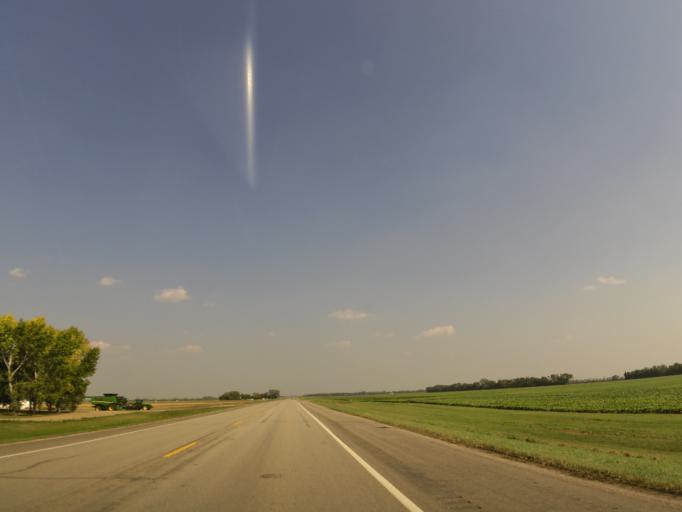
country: US
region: North Dakota
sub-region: Walsh County
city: Grafton
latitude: 48.4118
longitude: -97.2211
